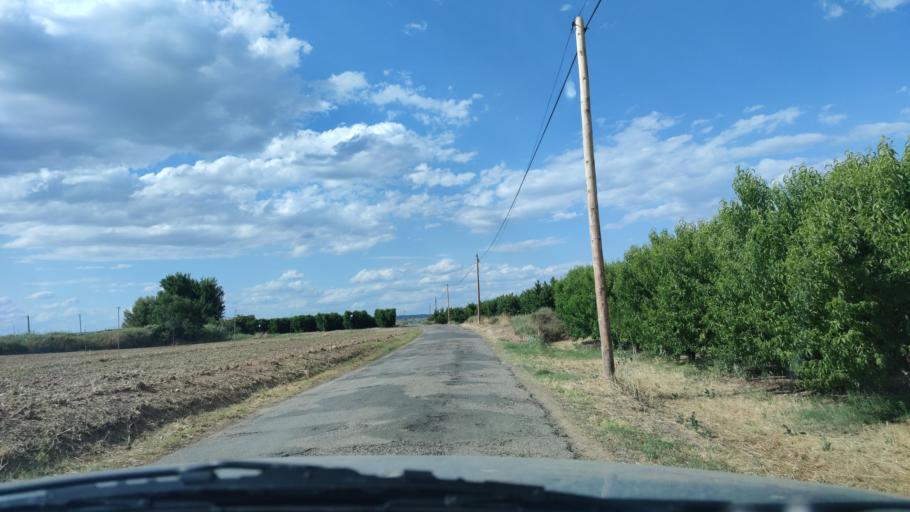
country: ES
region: Catalonia
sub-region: Provincia de Lleida
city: Alcarras
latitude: 41.5815
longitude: 0.5323
